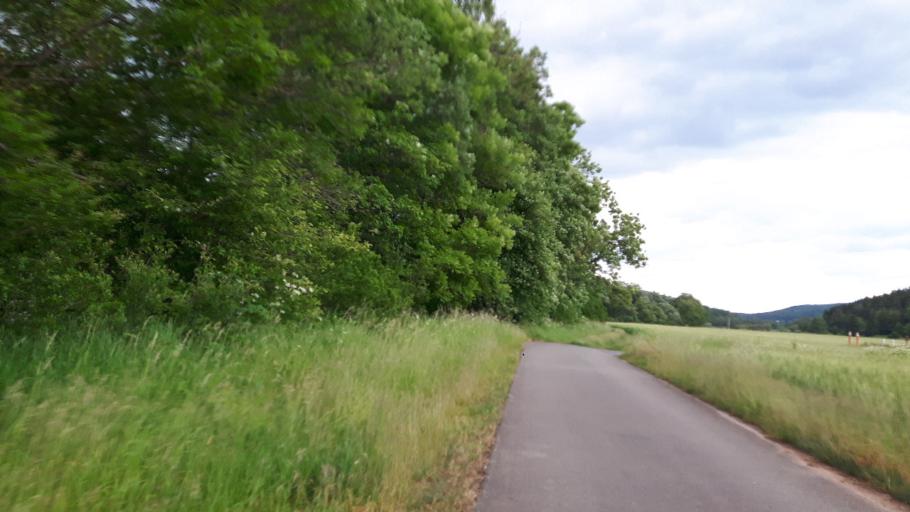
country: DE
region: Thuringia
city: Bad Berka
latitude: 50.8768
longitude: 11.2618
